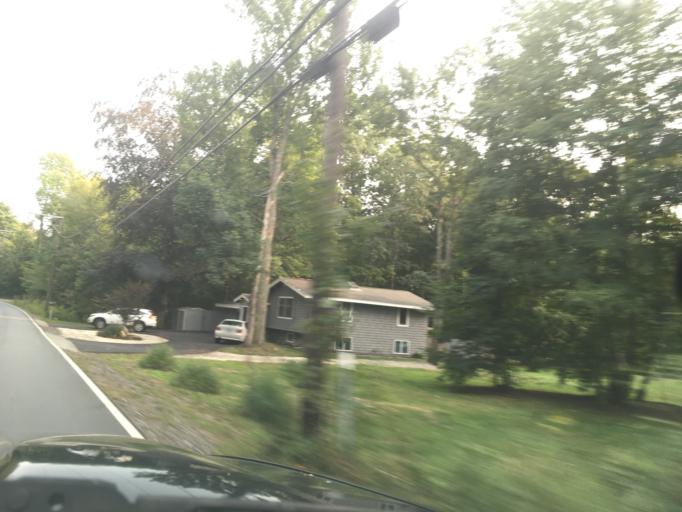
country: US
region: New Hampshire
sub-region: Rockingham County
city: Stratham Station
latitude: 43.0189
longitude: -70.8945
